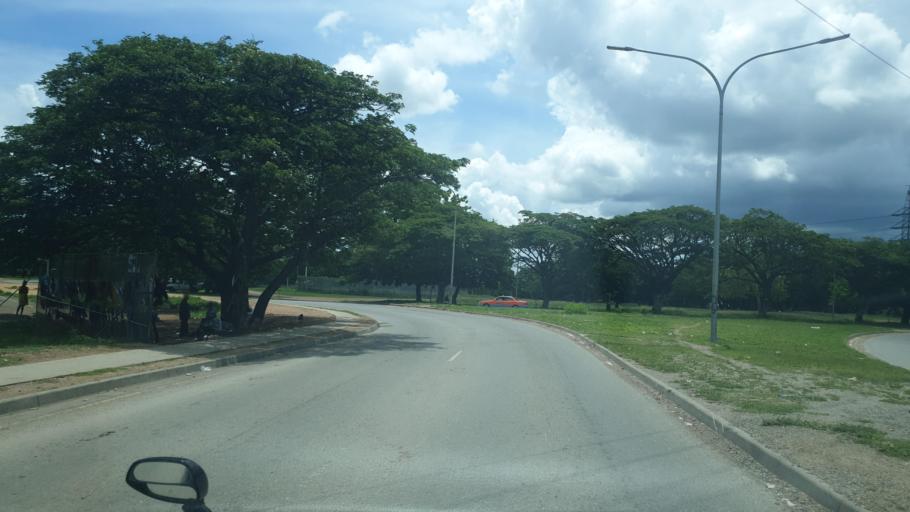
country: PG
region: National Capital
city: Port Moresby
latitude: -9.3965
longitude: 147.1578
